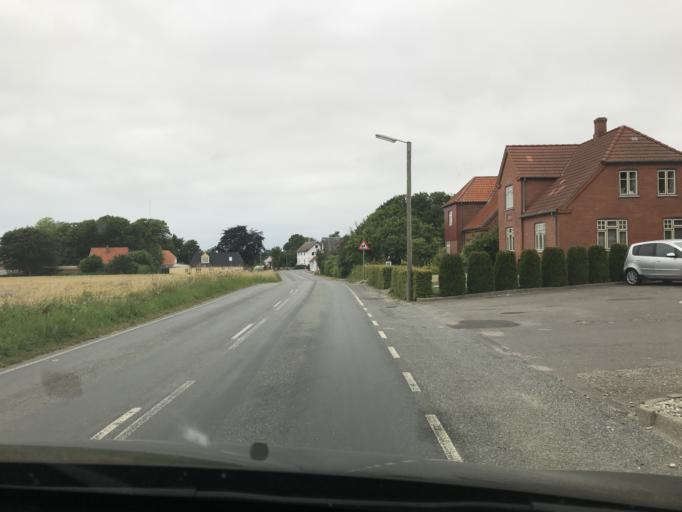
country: DK
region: South Denmark
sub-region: AEro Kommune
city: AEroskobing
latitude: 54.8474
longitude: 10.4221
